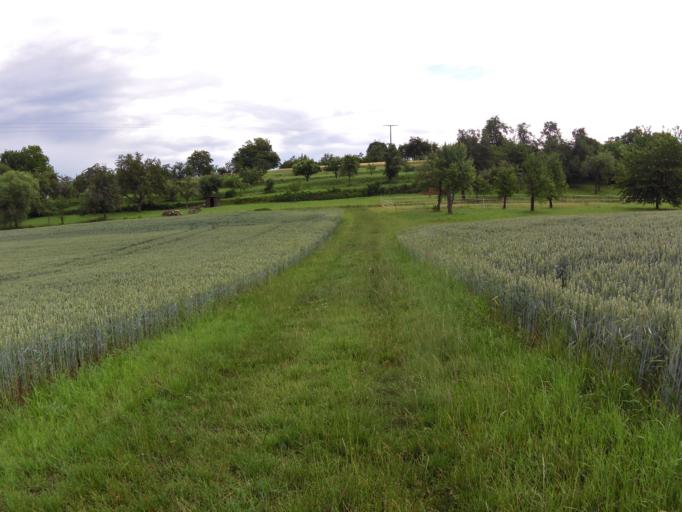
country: DE
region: Bavaria
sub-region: Regierungsbezirk Unterfranken
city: Erlabrunn
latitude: 49.8525
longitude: 9.8480
